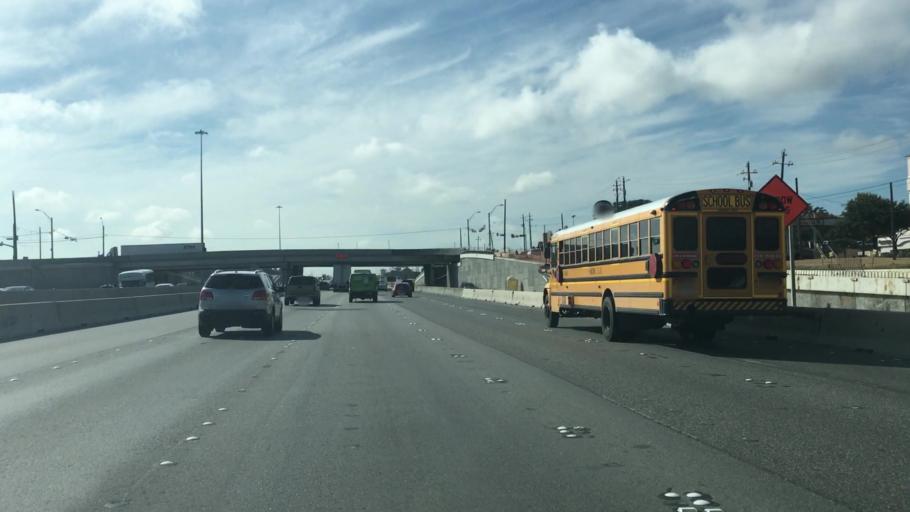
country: US
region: Texas
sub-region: Travis County
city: Onion Creek
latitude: 30.2007
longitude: -97.7636
